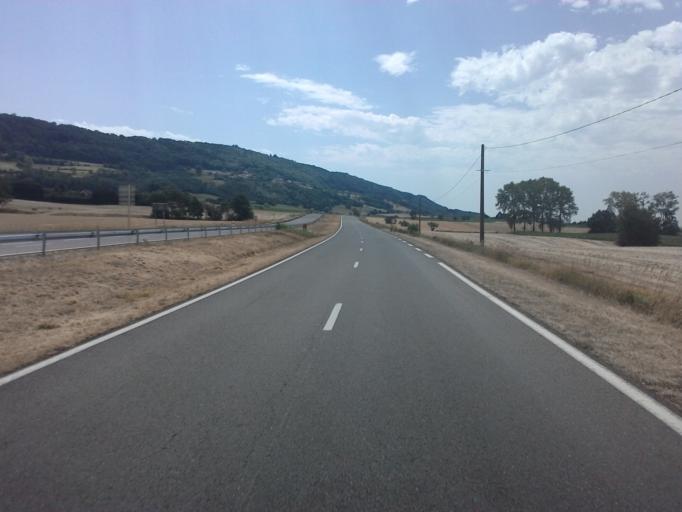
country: FR
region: Franche-Comte
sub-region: Departement du Jura
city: Saint-Amour
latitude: 46.4211
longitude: 5.3500
